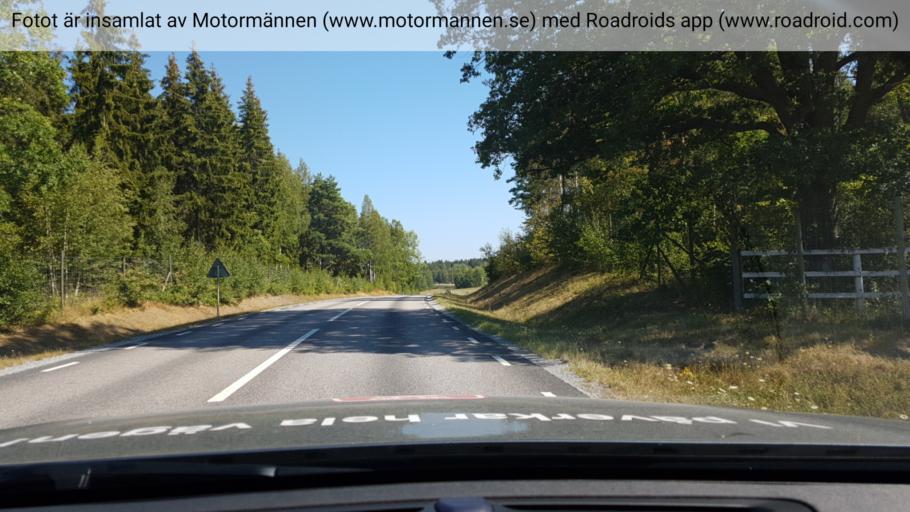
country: SE
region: Stockholm
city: Stenhamra
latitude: 59.3267
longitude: 17.6342
